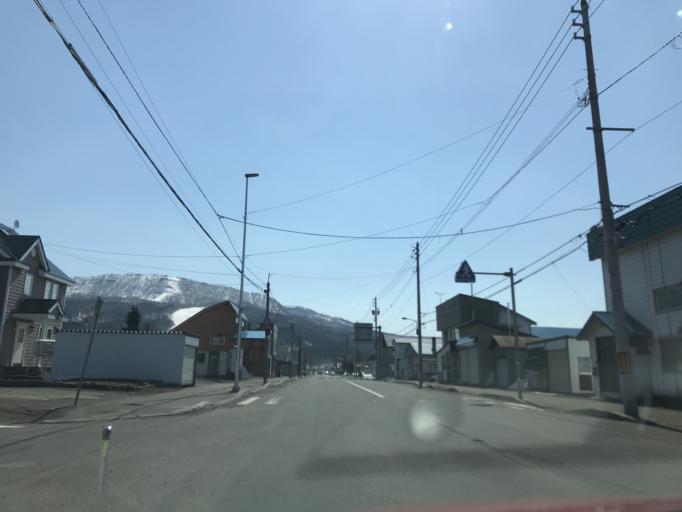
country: JP
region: Hokkaido
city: Nayoro
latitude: 44.7274
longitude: 142.2597
